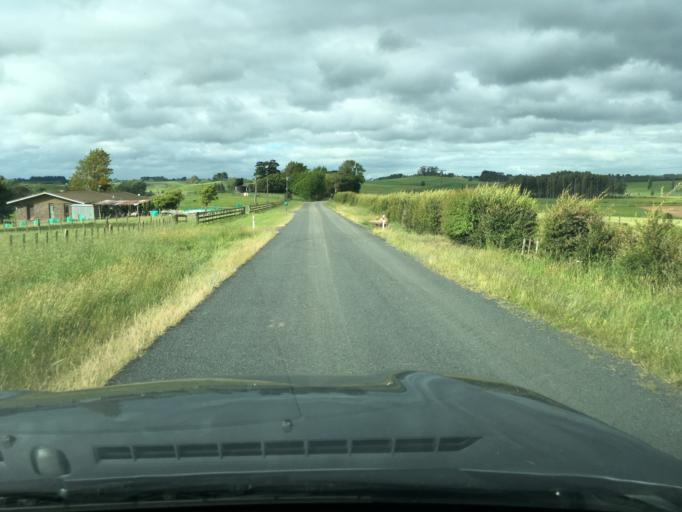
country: NZ
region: Waikato
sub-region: Hamilton City
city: Hamilton
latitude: -37.8201
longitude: 175.1781
